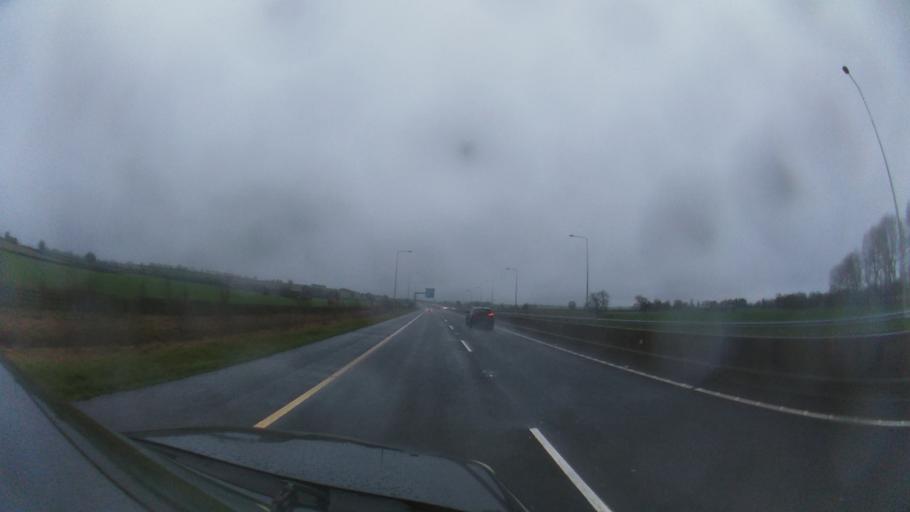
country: IE
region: Leinster
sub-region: Kildare
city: Castledermot
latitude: 52.9002
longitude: -6.8615
